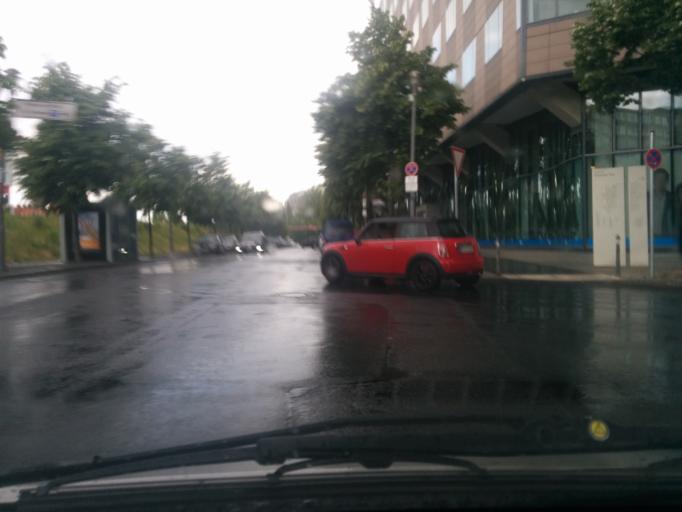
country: DE
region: Berlin
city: Tiergarten Bezirk
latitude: 52.5058
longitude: 13.3743
